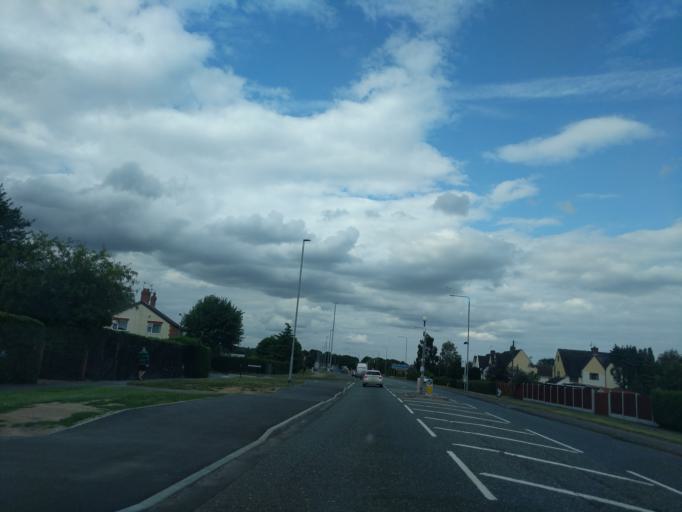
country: GB
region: England
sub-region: Nottinghamshire
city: Newark on Trent
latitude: 53.0892
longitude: -0.7932
